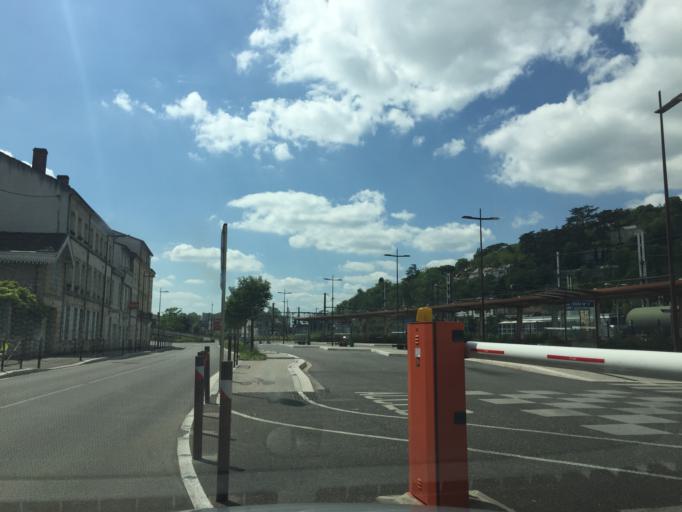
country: FR
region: Aquitaine
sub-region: Departement du Lot-et-Garonne
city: Agen
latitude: 44.2081
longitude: 0.6200
